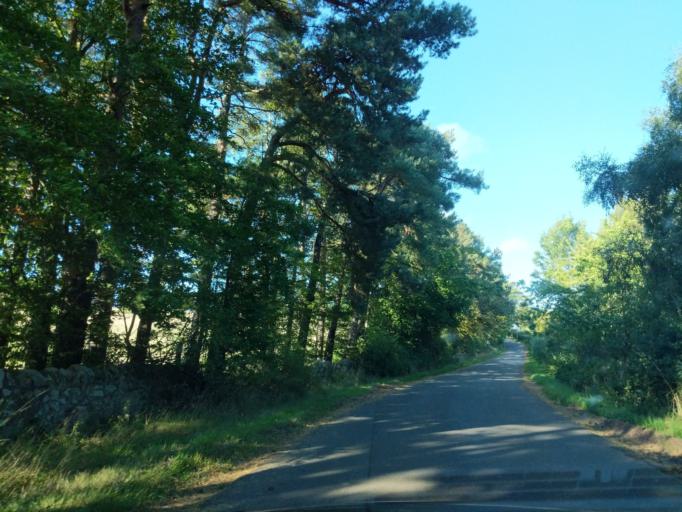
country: GB
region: Scotland
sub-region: East Lothian
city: Haddington
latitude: 55.9401
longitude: -2.7536
